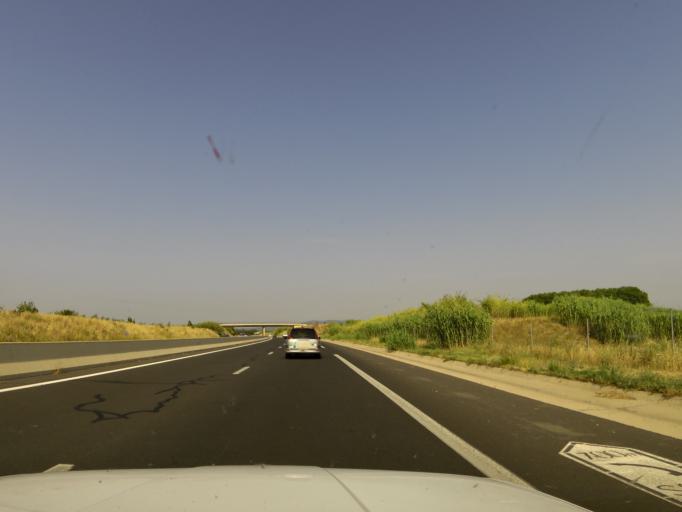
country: FR
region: Languedoc-Roussillon
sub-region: Departement de l'Herault
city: Saint-Andre-de-Sangonis
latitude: 43.6585
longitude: 3.4943
